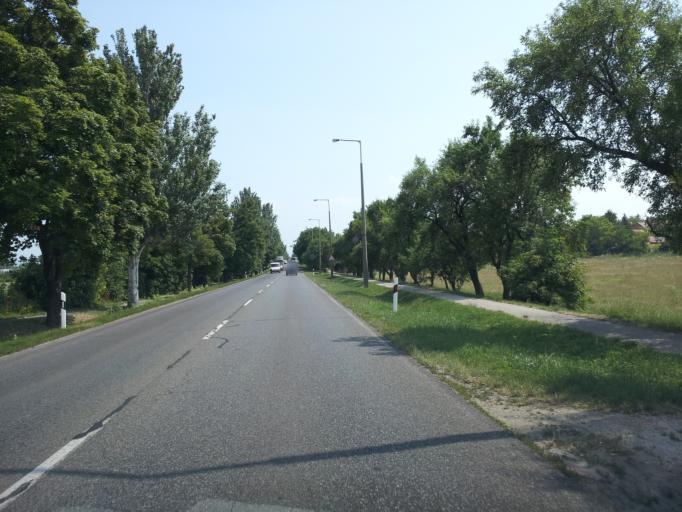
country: HU
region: Veszprem
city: Balatonalmadi
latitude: 47.0438
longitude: 18.0146
